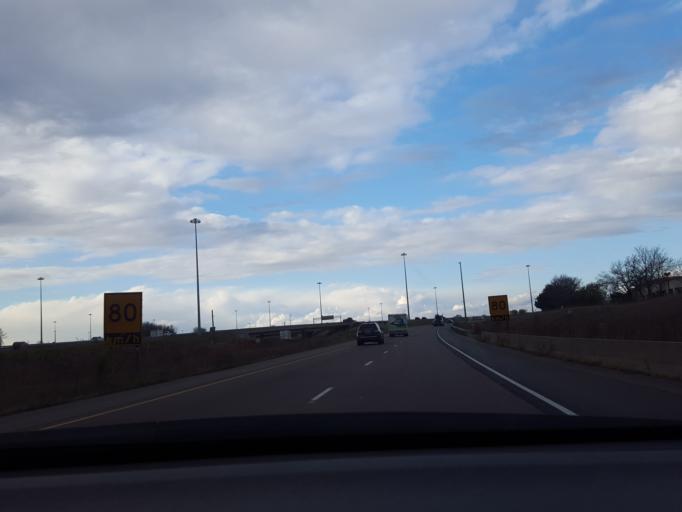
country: CA
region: Ontario
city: Mississauga
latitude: 43.6341
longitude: -79.6513
